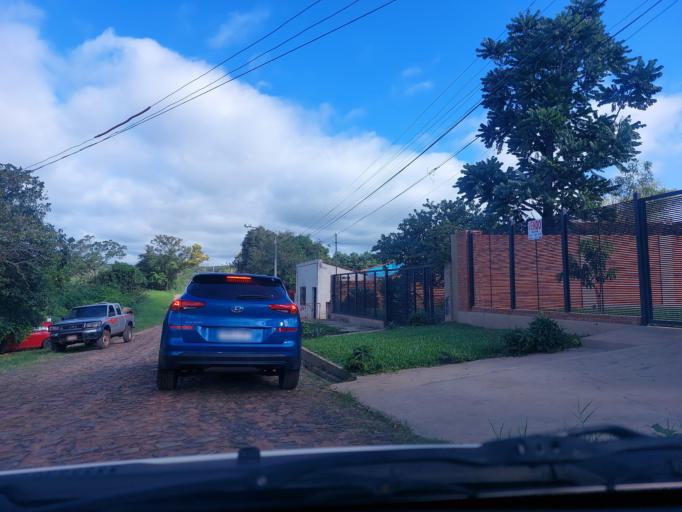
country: PY
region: San Pedro
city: Guayaybi
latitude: -24.6676
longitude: -56.4360
